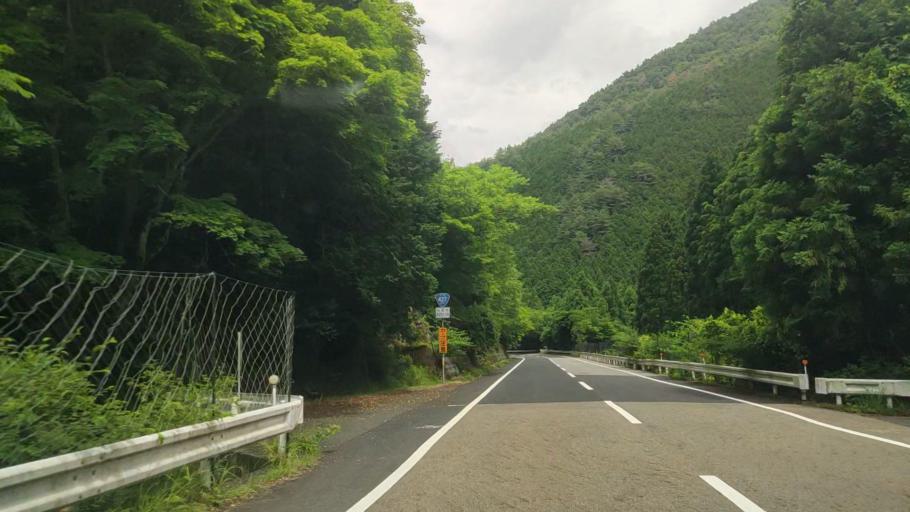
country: JP
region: Kyoto
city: Fukuchiyama
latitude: 35.2262
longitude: 134.9508
